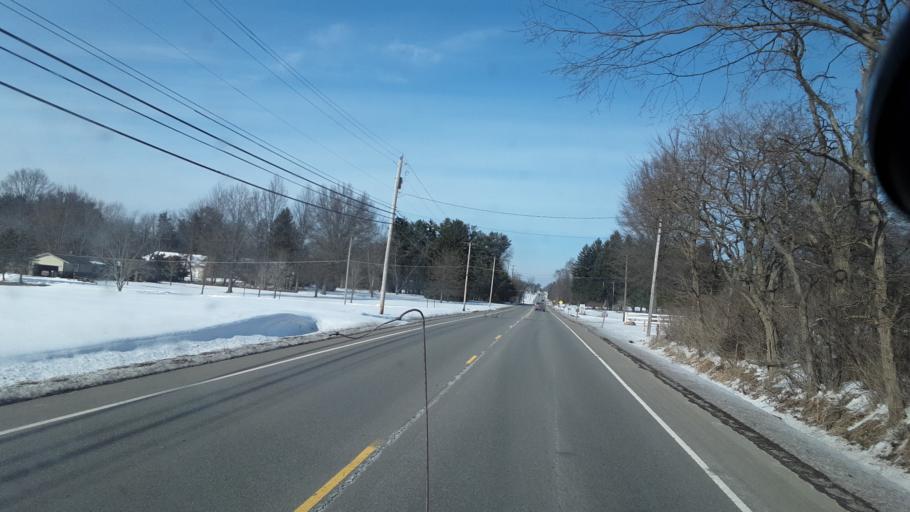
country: US
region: Ohio
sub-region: Mahoning County
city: Canfield
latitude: 40.9986
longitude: -80.7607
